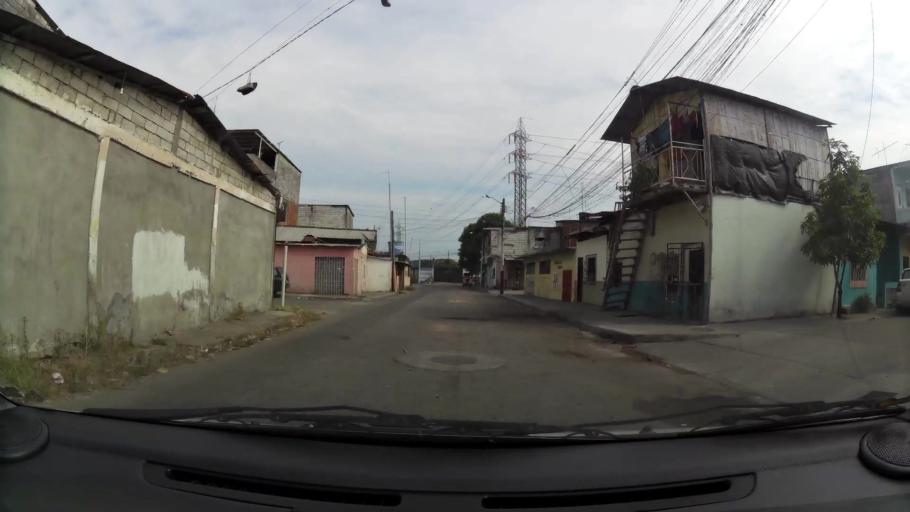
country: EC
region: Guayas
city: Guayaquil
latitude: -2.2566
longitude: -79.9065
